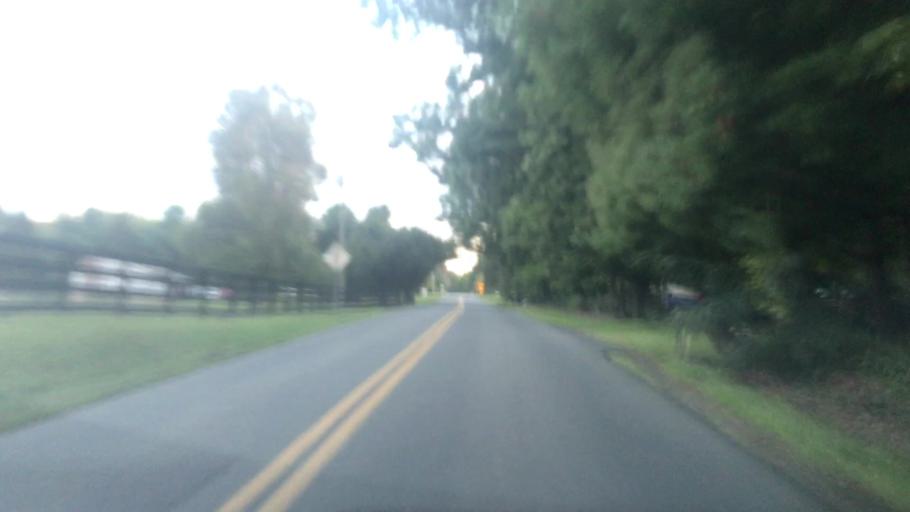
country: US
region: Virginia
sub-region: Prince William County
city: Nokesville
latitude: 38.7067
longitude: -77.6656
